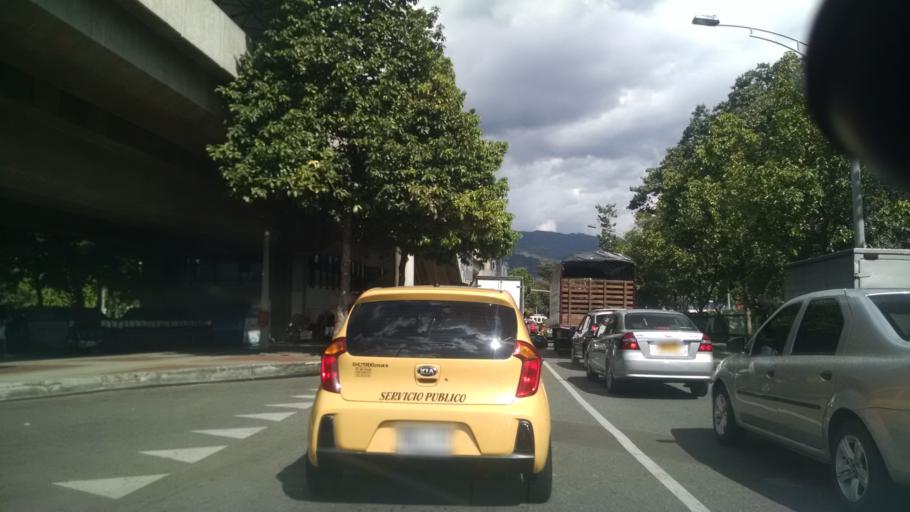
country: CO
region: Antioquia
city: Medellin
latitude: 6.2529
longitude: -75.5834
